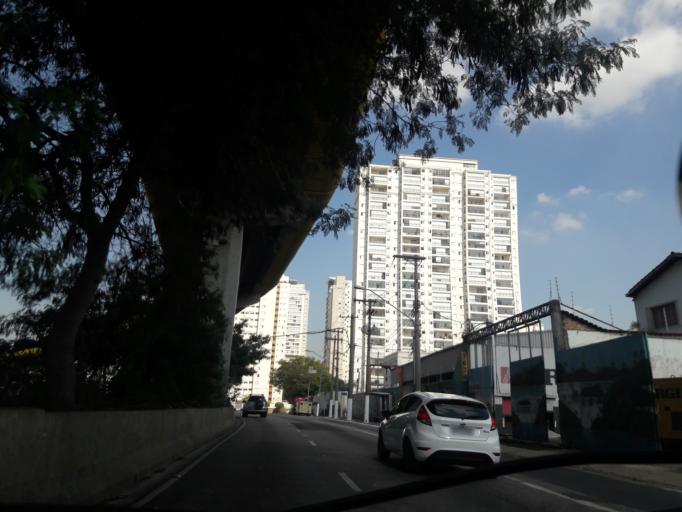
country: BR
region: Sao Paulo
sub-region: Sao Paulo
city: Sao Paulo
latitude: -23.5726
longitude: -46.6043
